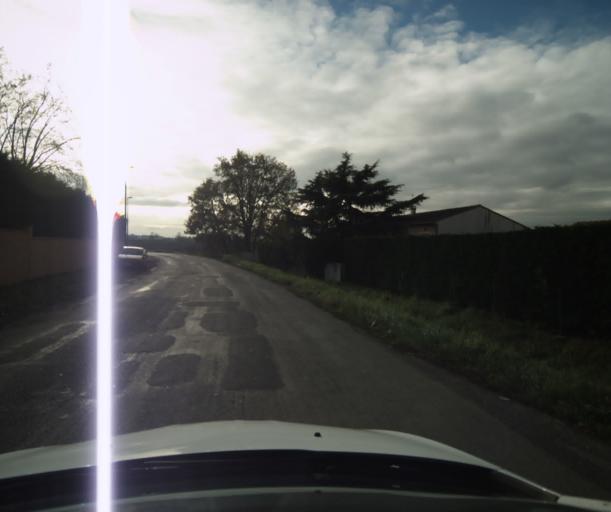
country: FR
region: Midi-Pyrenees
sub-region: Departement de la Haute-Garonne
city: Bruguieres
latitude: 43.7329
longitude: 1.4019
